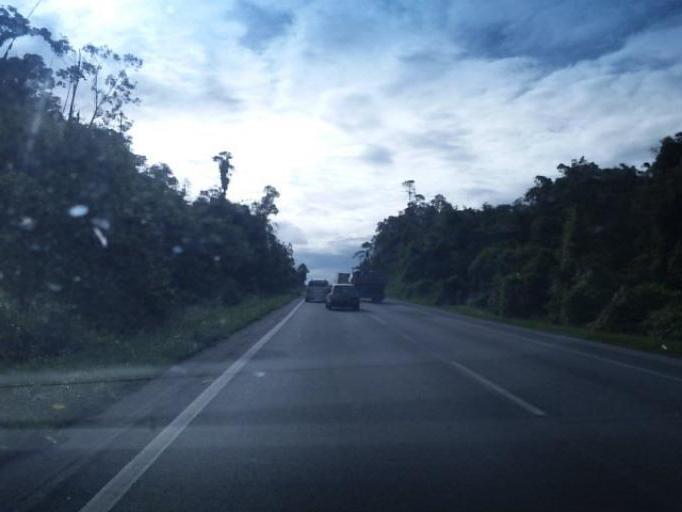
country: BR
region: Parana
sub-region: Antonina
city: Antonina
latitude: -25.1084
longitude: -48.7705
